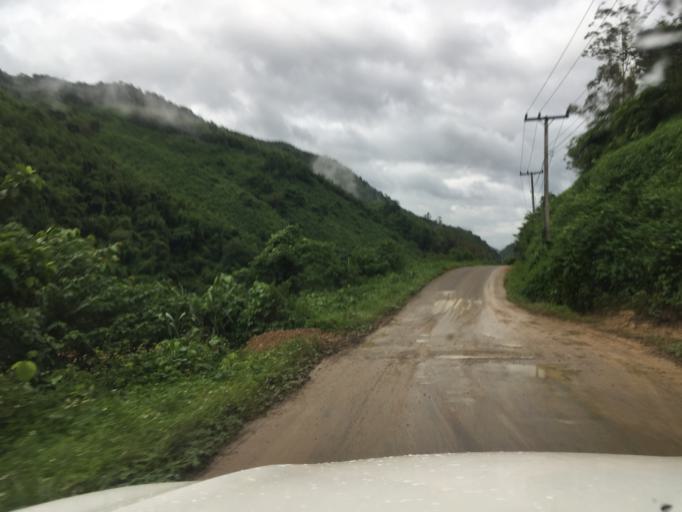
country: LA
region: Oudomxai
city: Muang La
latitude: 20.9954
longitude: 102.2308
